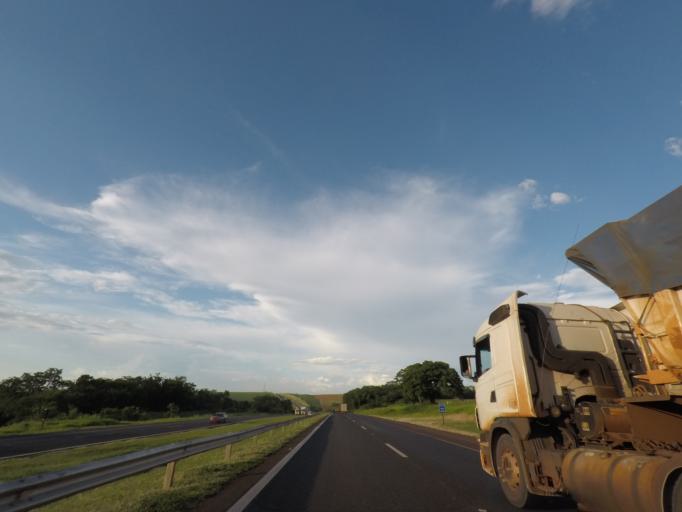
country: BR
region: Sao Paulo
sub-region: Ituverava
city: Ituverava
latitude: -20.2928
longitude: -47.7982
